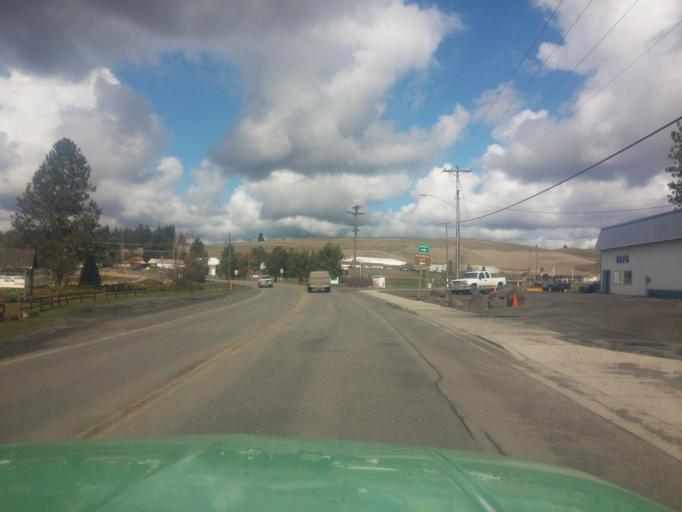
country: US
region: Idaho
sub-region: Latah County
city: Moscow
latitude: 46.9248
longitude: -116.9026
